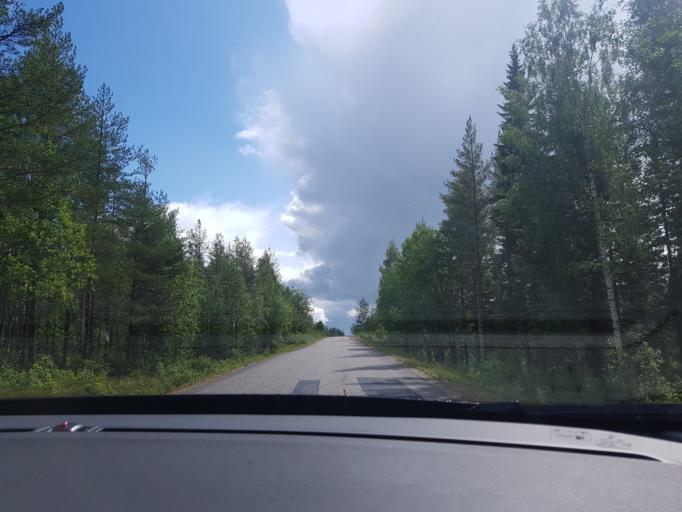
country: FI
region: Kainuu
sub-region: Kehys-Kainuu
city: Kuhmo
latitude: 64.4583
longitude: 29.6422
